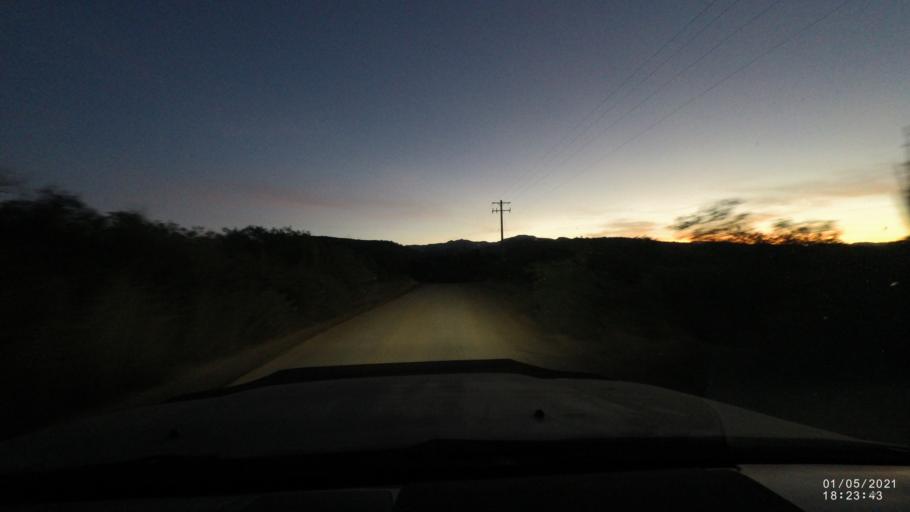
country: BO
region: Cochabamba
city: Capinota
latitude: -17.6588
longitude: -66.2402
